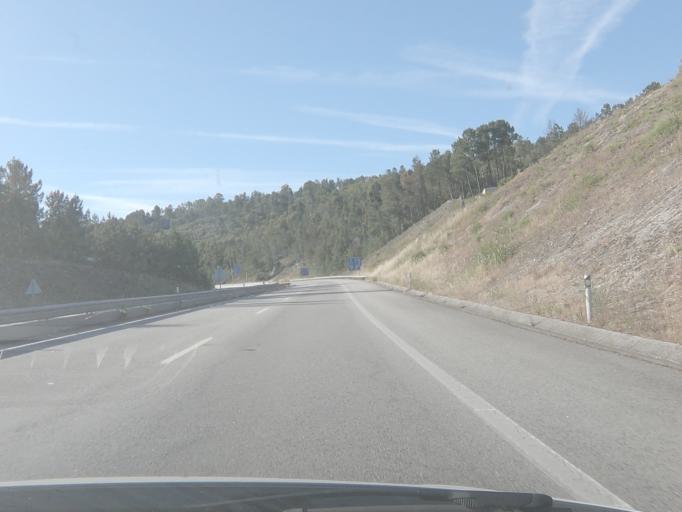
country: PT
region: Viseu
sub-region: Viseu
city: Campo
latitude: 40.8032
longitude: -7.9316
